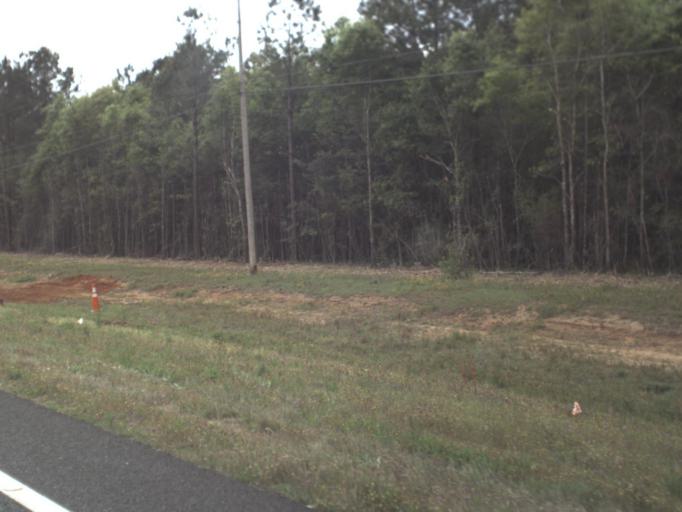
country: US
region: Florida
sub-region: Escambia County
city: Century
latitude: 30.9262
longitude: -87.3073
